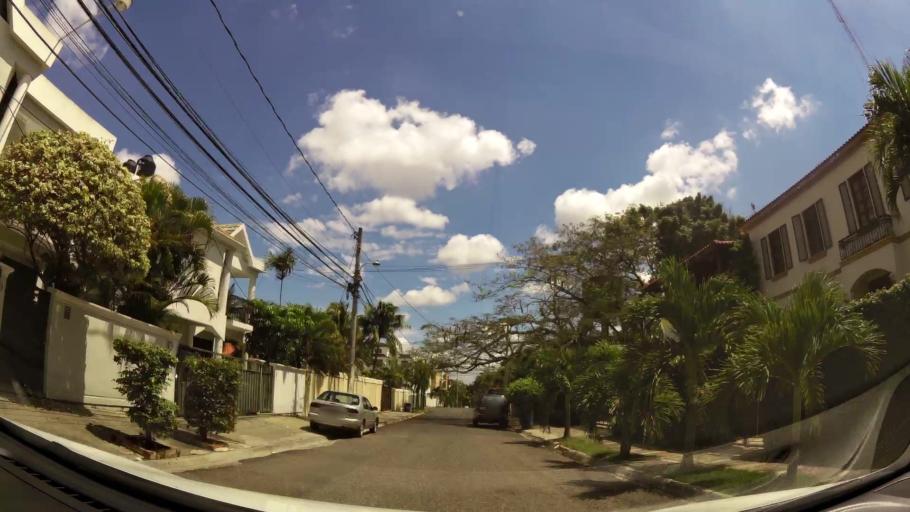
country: DO
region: Santiago
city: Santiago de los Caballeros
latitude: 19.4682
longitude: -70.6754
